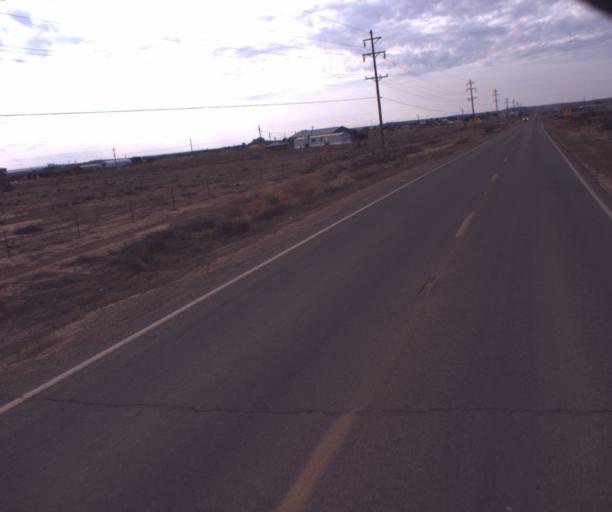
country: US
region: Arizona
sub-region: Apache County
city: Many Farms
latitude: 36.3589
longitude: -109.6155
